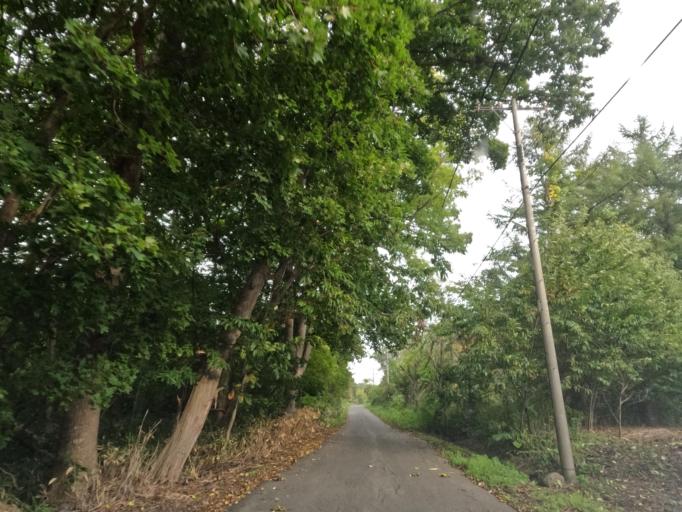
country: JP
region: Hokkaido
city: Date
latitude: 42.4125
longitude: 140.9223
